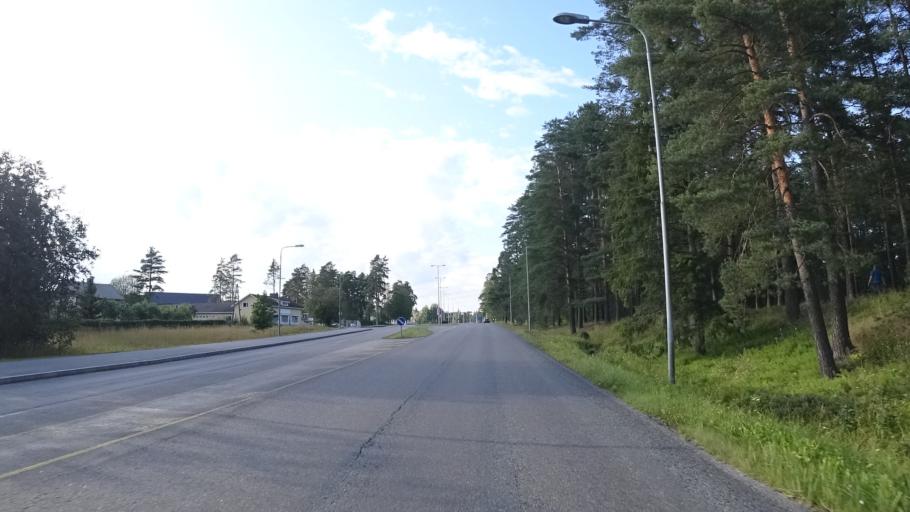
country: FI
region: South Karelia
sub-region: Imatra
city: Imatra
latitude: 61.1819
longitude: 28.7811
